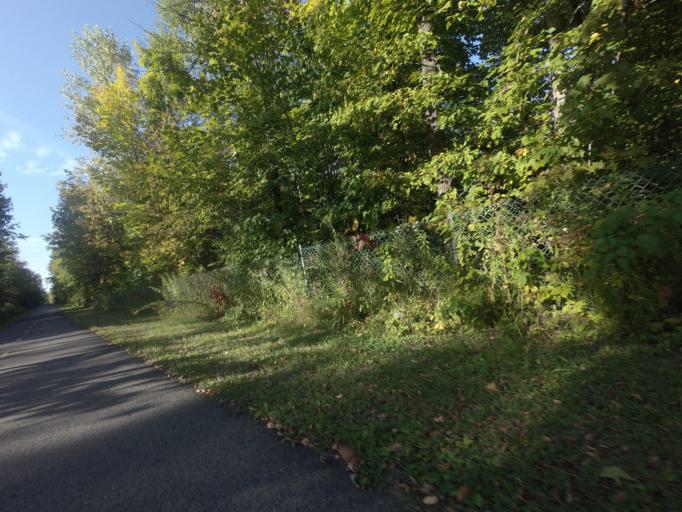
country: CA
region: Quebec
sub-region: Laurentides
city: Saint-Jerome
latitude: 45.7300
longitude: -73.9427
